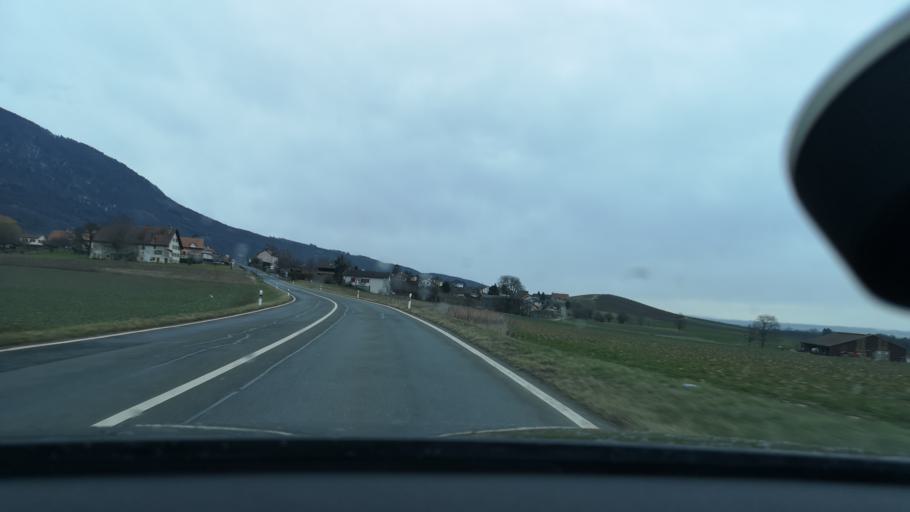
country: CH
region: Vaud
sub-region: Jura-Nord vaudois District
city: Grandson
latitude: 46.8351
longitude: 6.6856
